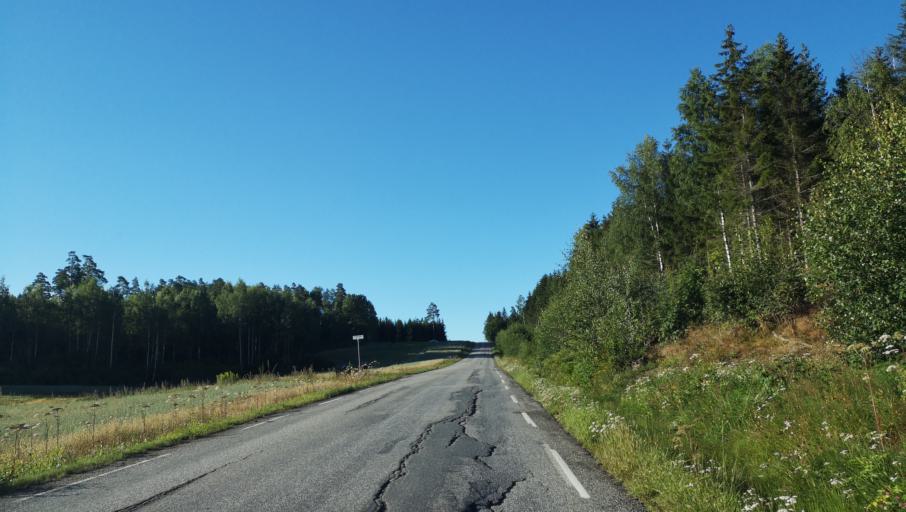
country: NO
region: Ostfold
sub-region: Hobol
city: Tomter
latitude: 59.6474
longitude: 11.0143
